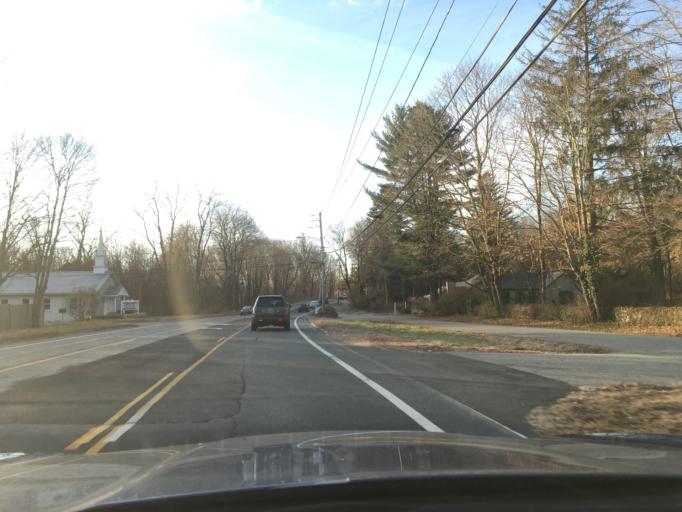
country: US
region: Rhode Island
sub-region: Washington County
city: North Kingstown
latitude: 41.5800
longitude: -71.4598
